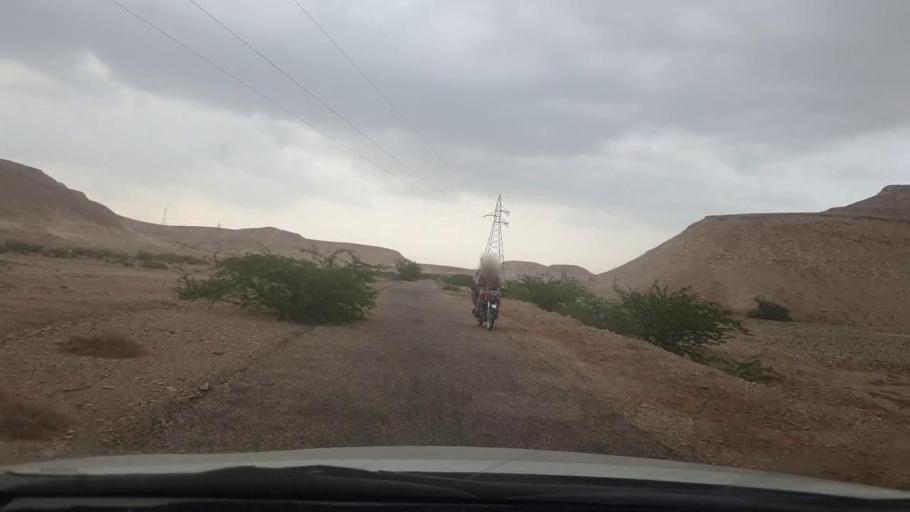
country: PK
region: Sindh
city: Khairpur
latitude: 27.4662
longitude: 68.9225
